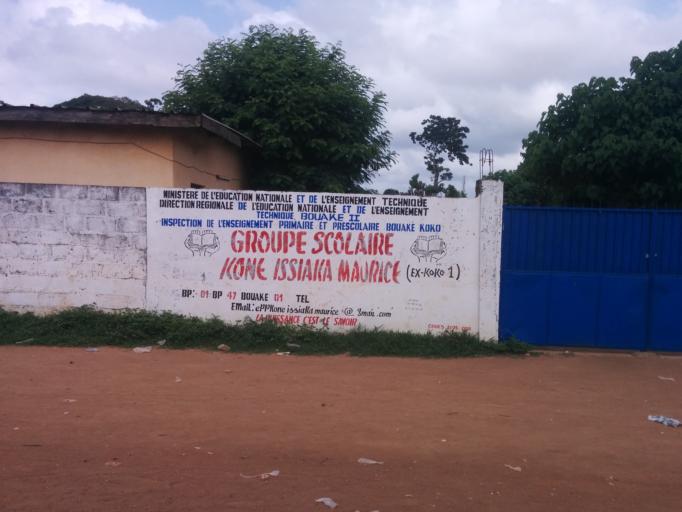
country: CI
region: Vallee du Bandama
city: Bouake
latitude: 7.6873
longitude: -5.0376
